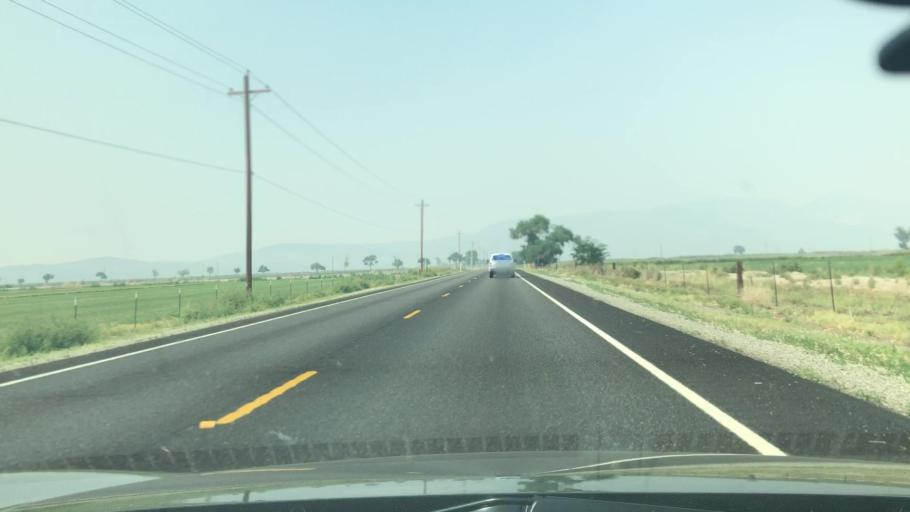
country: US
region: Nevada
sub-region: Lyon County
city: Yerington
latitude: 39.1225
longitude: -119.1810
